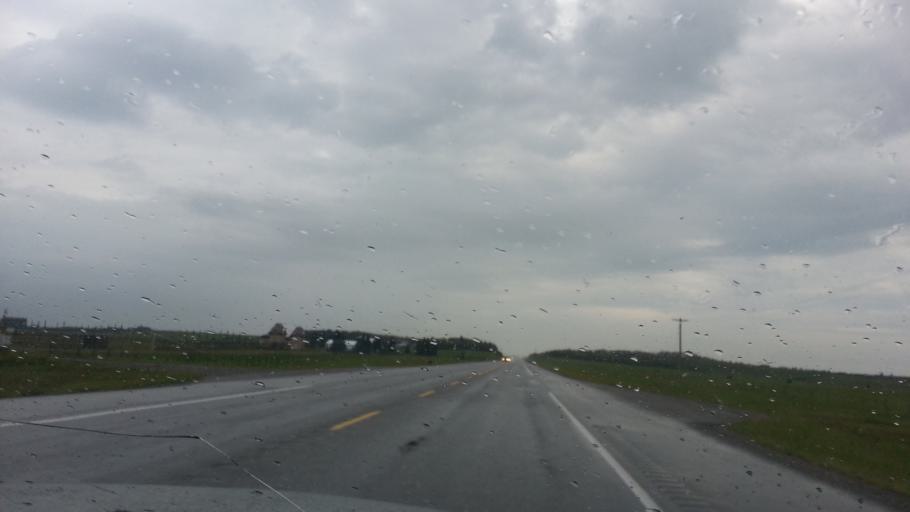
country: CA
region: Alberta
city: Cochrane
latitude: 51.0449
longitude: -114.4668
